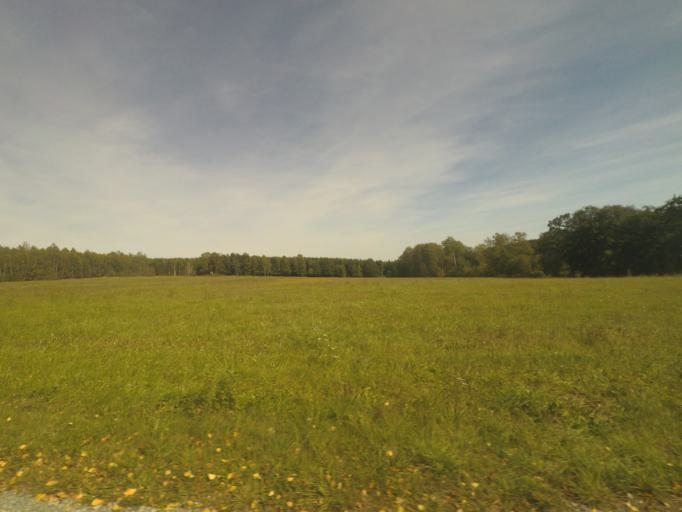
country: DE
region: Thuringia
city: Christes
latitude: 50.6432
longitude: 10.4661
